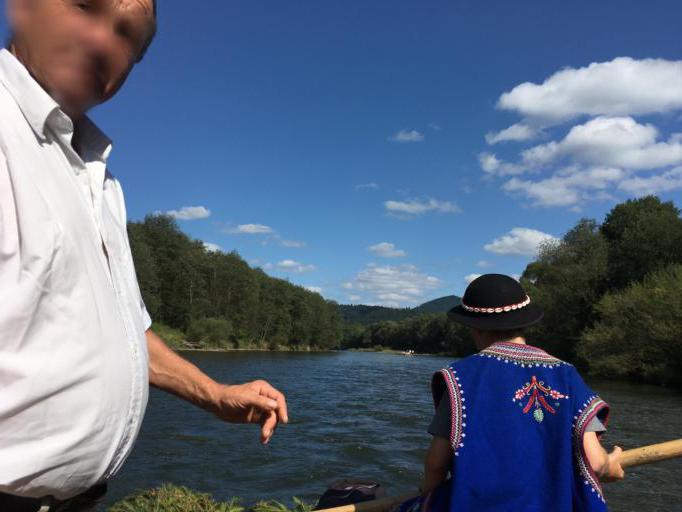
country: PL
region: Lesser Poland Voivodeship
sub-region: Powiat nowotarski
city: Kroscienko nad Dunajcem
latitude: 49.3889
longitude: 20.3894
